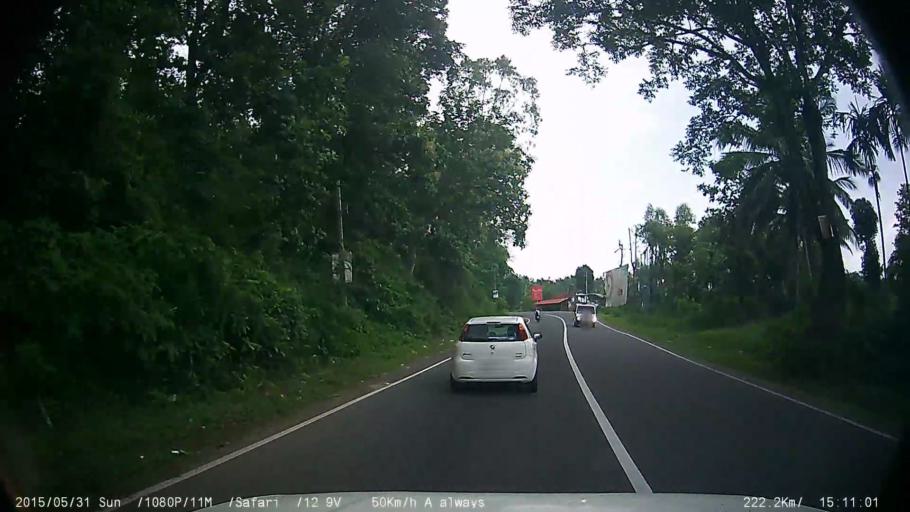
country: IN
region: Kerala
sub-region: Wayanad
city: Panamaram
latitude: 11.6606
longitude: 76.2287
